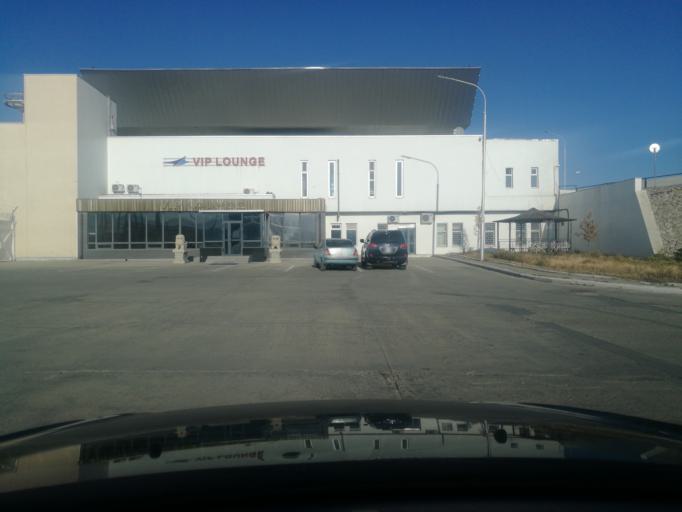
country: MN
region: Ulaanbaatar
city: Ulaanbaatar
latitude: 47.8518
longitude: 106.7641
